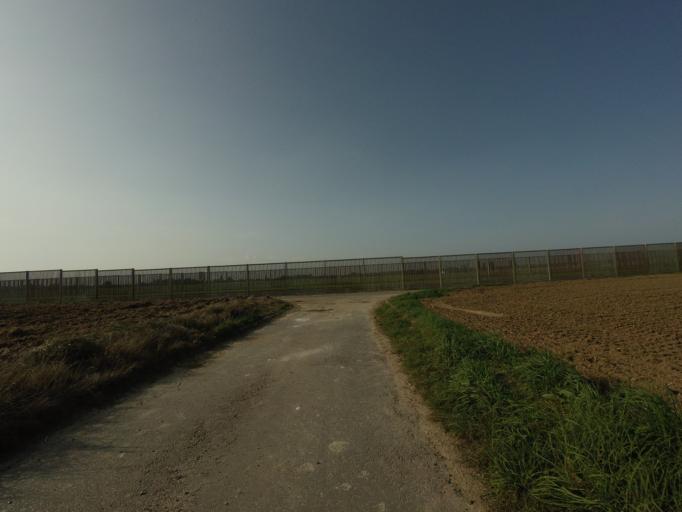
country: BE
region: Flanders
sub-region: Provincie Vlaams-Brabant
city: Kortenberg
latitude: 50.8974
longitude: 4.5248
